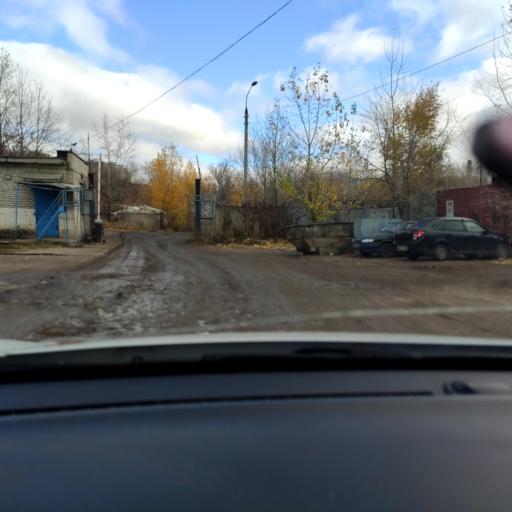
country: RU
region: Tatarstan
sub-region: Gorod Kazan'
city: Kazan
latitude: 55.7777
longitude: 49.1825
